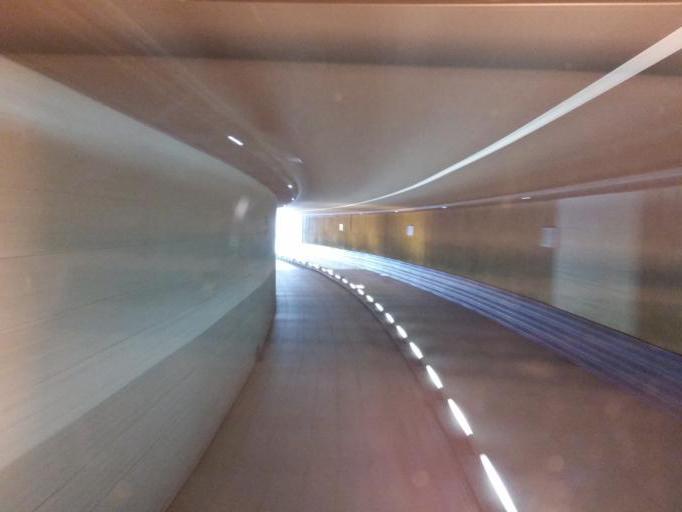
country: DE
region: Baden-Wuerttemberg
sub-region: Freiburg Region
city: Konstanz
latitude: 47.6518
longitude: 9.1733
